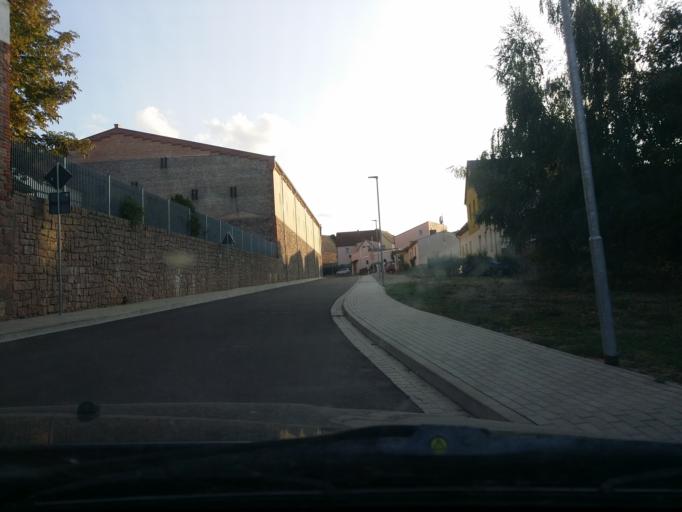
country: DE
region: Saxony-Anhalt
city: Petersberg
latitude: 51.6104
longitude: 11.9350
